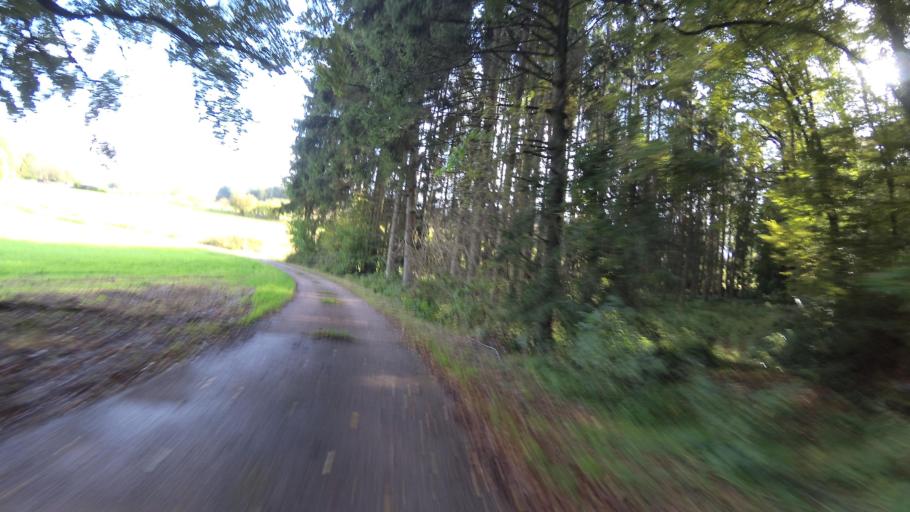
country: DE
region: Rheinland-Pfalz
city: Frohnhofen
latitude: 49.4496
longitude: 7.3100
